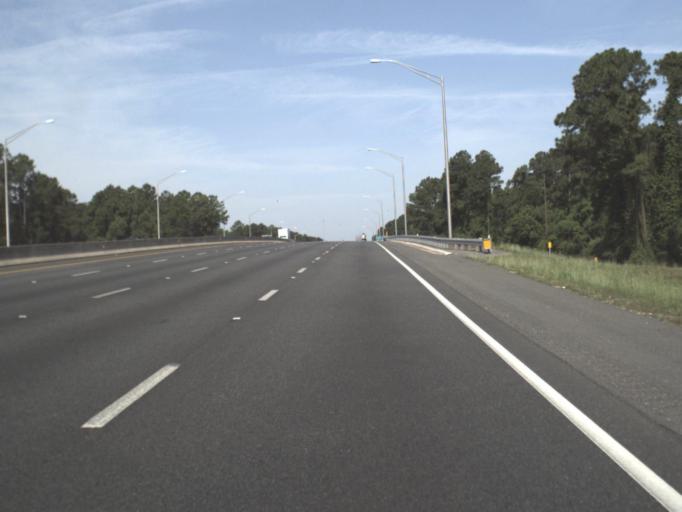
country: US
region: Florida
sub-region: Saint Johns County
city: Ponte Vedra Beach
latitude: 30.2514
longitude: -81.4818
